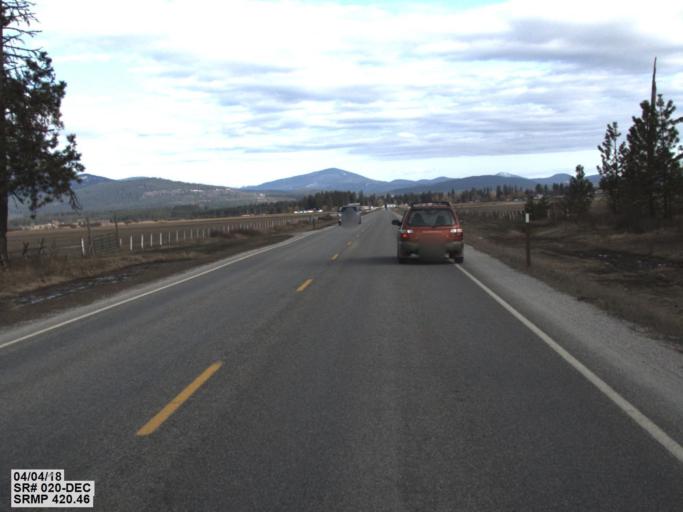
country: US
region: Washington
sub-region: Pend Oreille County
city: Newport
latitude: 48.3184
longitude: -117.2928
